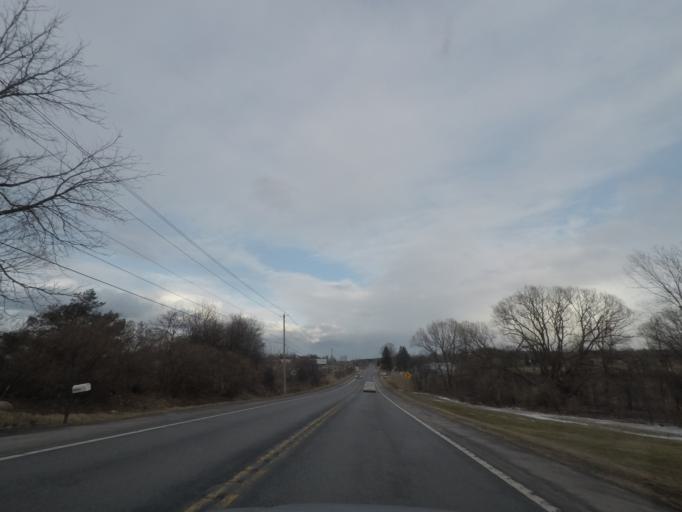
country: US
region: New York
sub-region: Oneida County
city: Vernon
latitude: 43.0748
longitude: -75.4617
